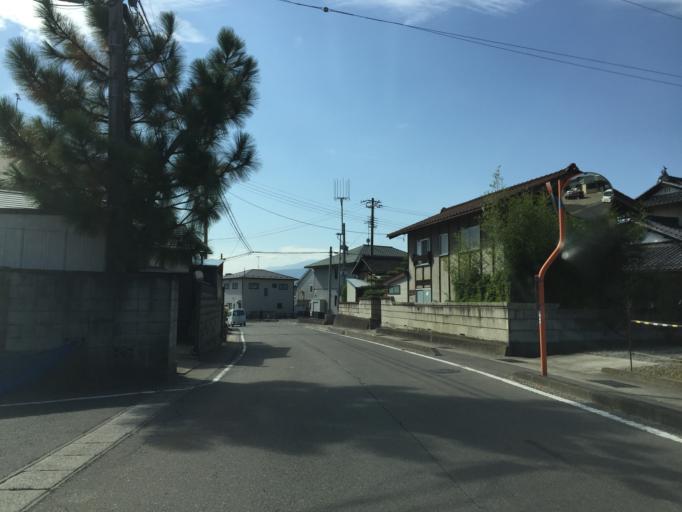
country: JP
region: Fukushima
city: Fukushima-shi
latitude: 37.7379
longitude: 140.4498
